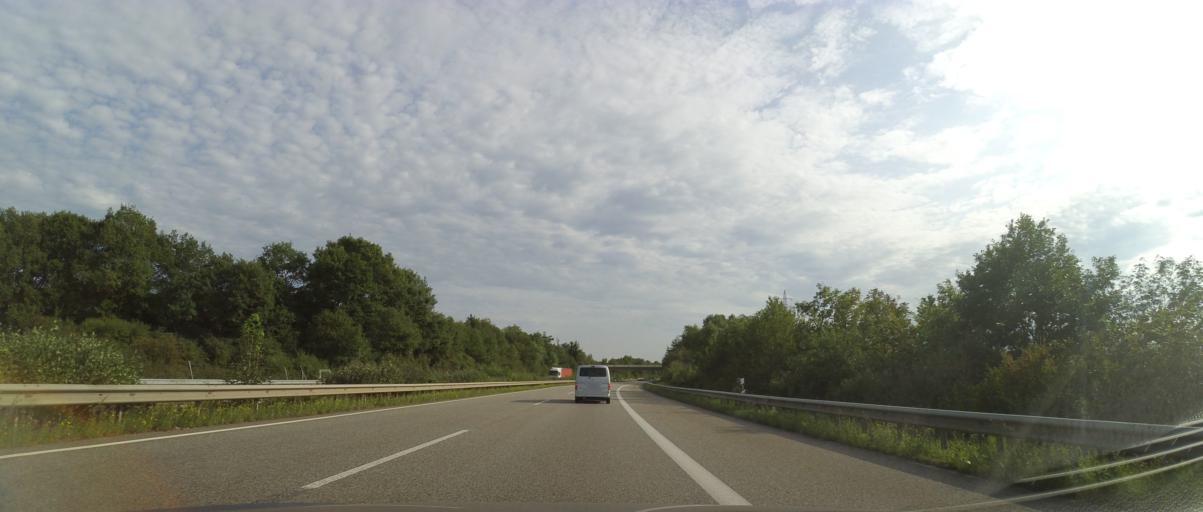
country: DE
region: Rheinland-Pfalz
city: Flussbach
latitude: 50.0192
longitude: 6.9394
